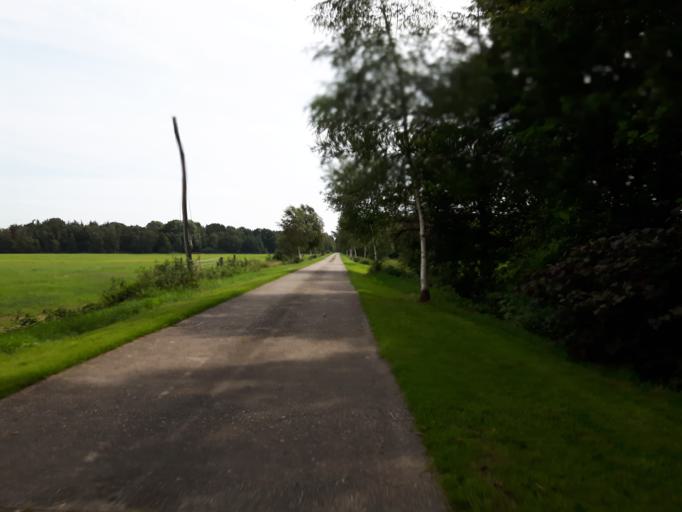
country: DE
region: Lower Saxony
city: Ovelgonne
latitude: 53.2974
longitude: 8.3135
